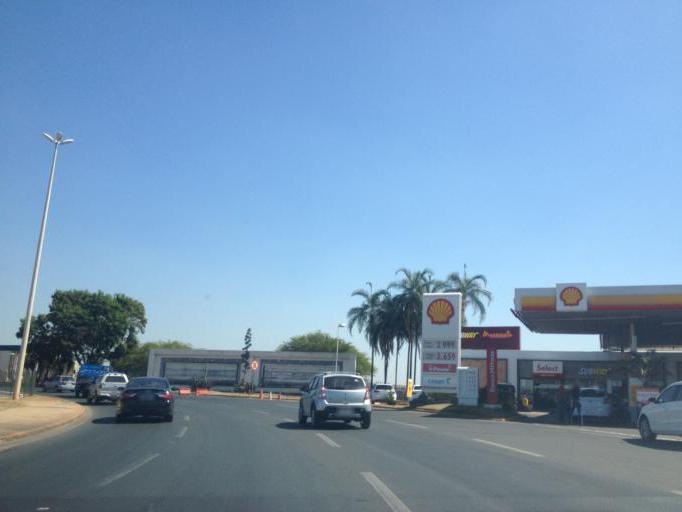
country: BR
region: Federal District
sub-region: Brasilia
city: Brasilia
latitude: -15.8679
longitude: -47.9240
